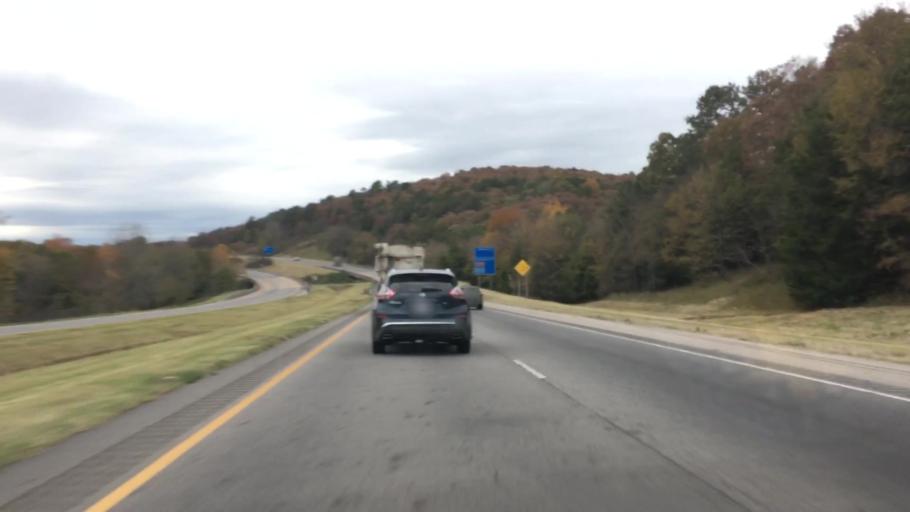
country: US
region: Arkansas
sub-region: Johnson County
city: Coal Hill
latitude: 35.5021
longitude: -93.7271
